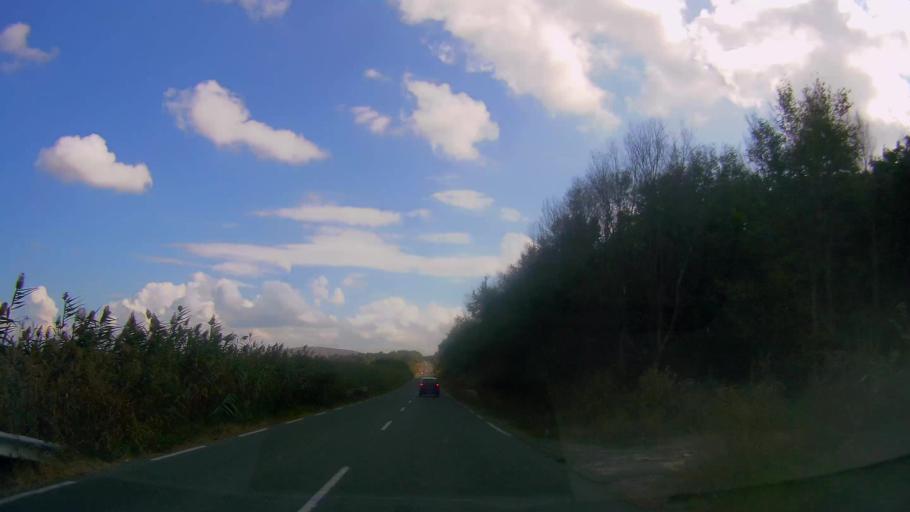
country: BG
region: Burgas
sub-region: Obshtina Kameno
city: Kameno
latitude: 42.4871
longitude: 27.3407
